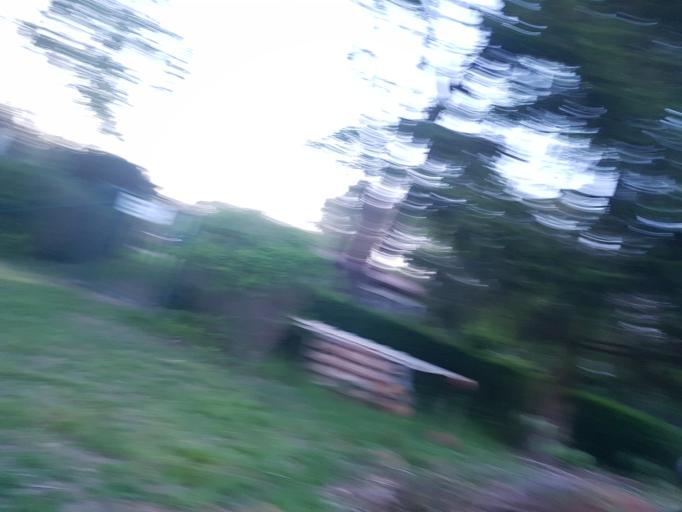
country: DE
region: Brandenburg
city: Bad Liebenwerda
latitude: 51.5525
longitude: 13.3688
